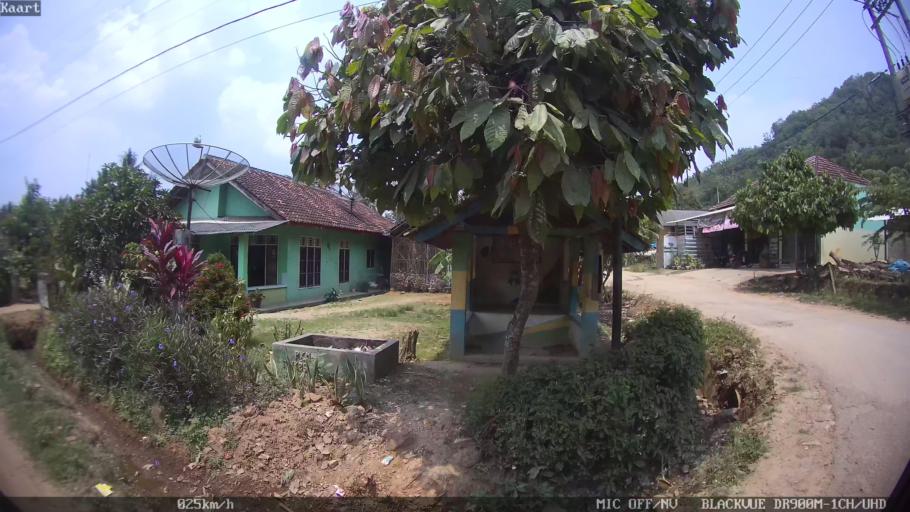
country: ID
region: Lampung
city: Pringsewu
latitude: -5.3815
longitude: 105.0003
